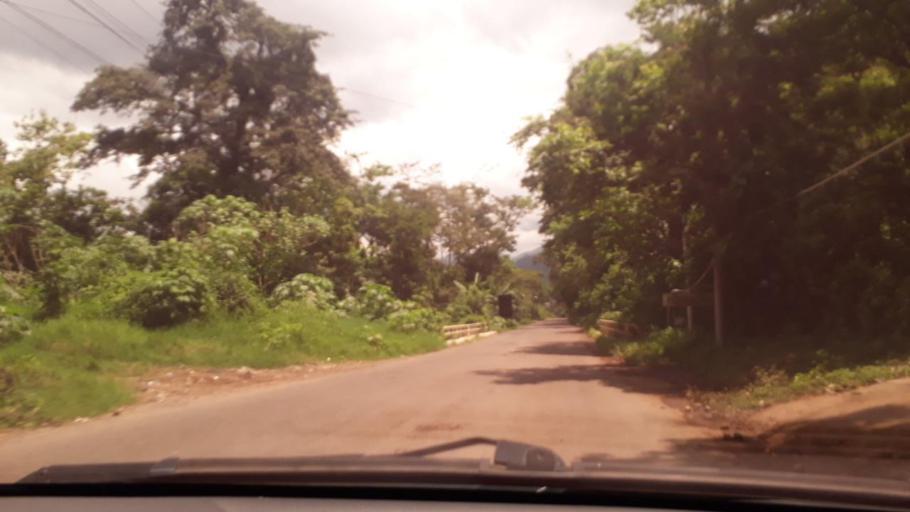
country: GT
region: Santa Rosa
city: Oratorio
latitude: 14.2388
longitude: -90.1974
